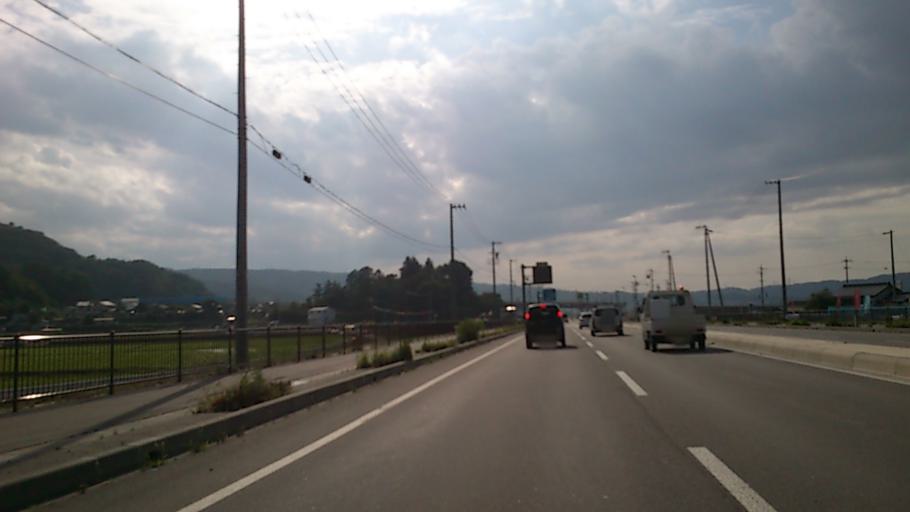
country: JP
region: Nagano
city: Saku
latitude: 36.2363
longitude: 138.4434
